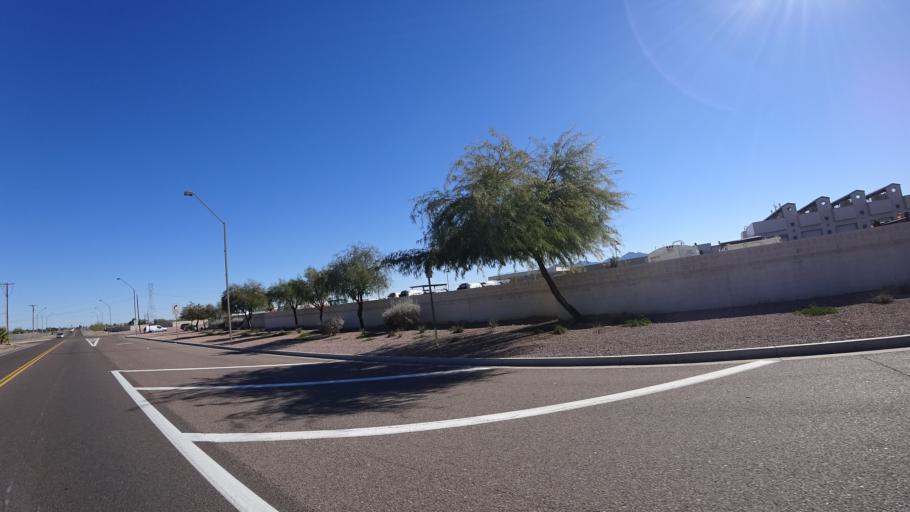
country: US
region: Arizona
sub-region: Maricopa County
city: Avondale
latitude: 33.4208
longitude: -112.3463
